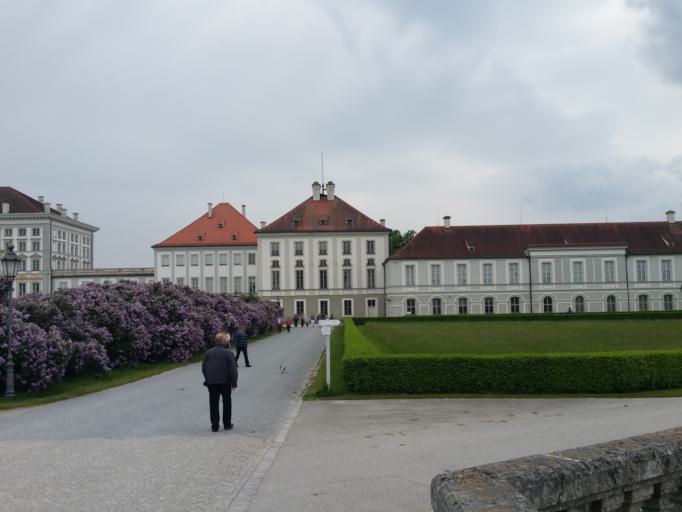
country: DE
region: Bavaria
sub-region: Upper Bavaria
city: Pasing
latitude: 48.1590
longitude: 11.5055
